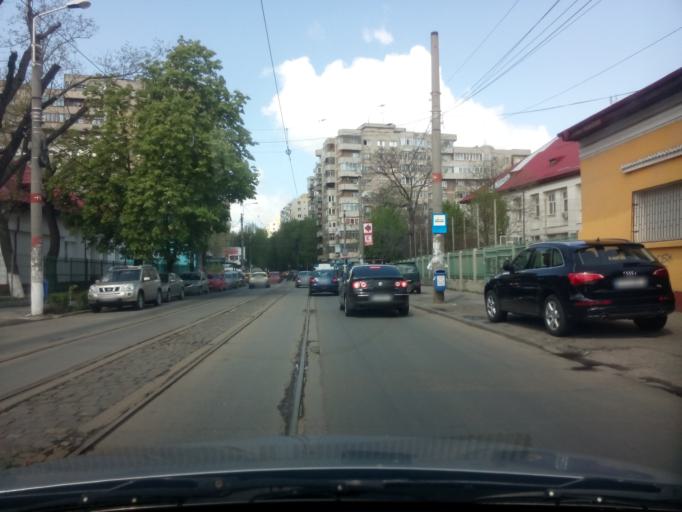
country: RO
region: Bucuresti
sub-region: Municipiul Bucuresti
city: Bucharest
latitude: 44.4609
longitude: 26.1194
